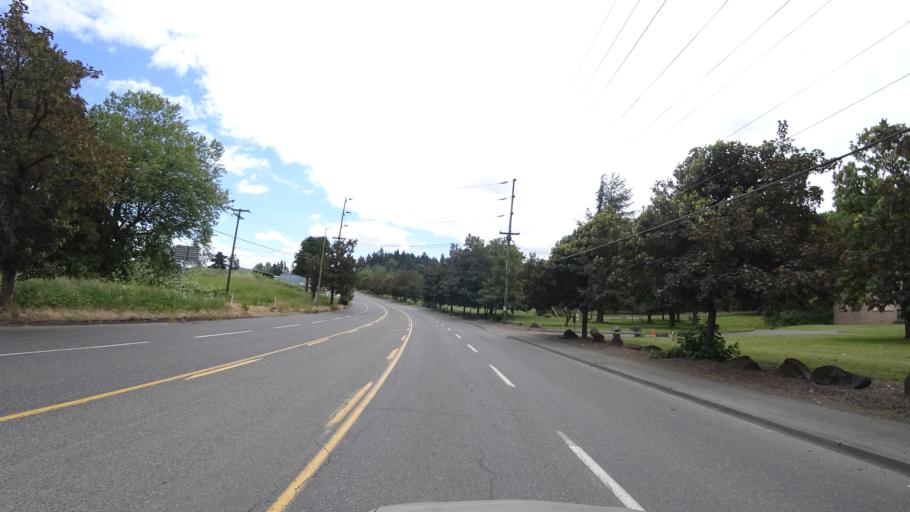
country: US
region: Oregon
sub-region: Washington County
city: West Haven
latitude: 45.6082
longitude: -122.7589
